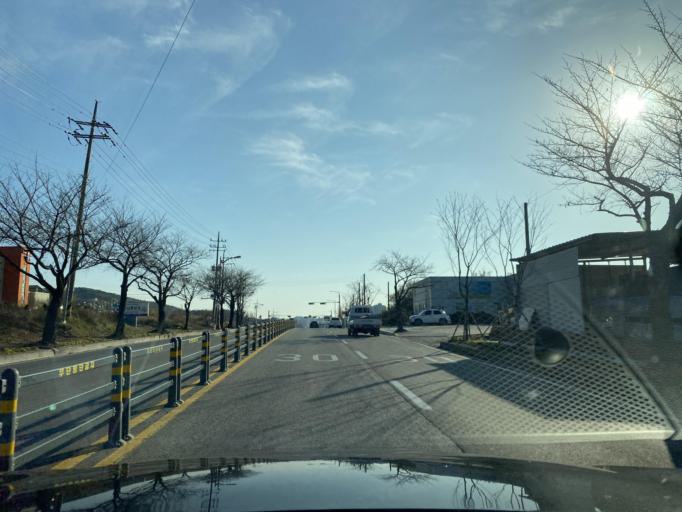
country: KR
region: Chungcheongnam-do
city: Yesan
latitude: 36.7053
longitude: 126.8391
